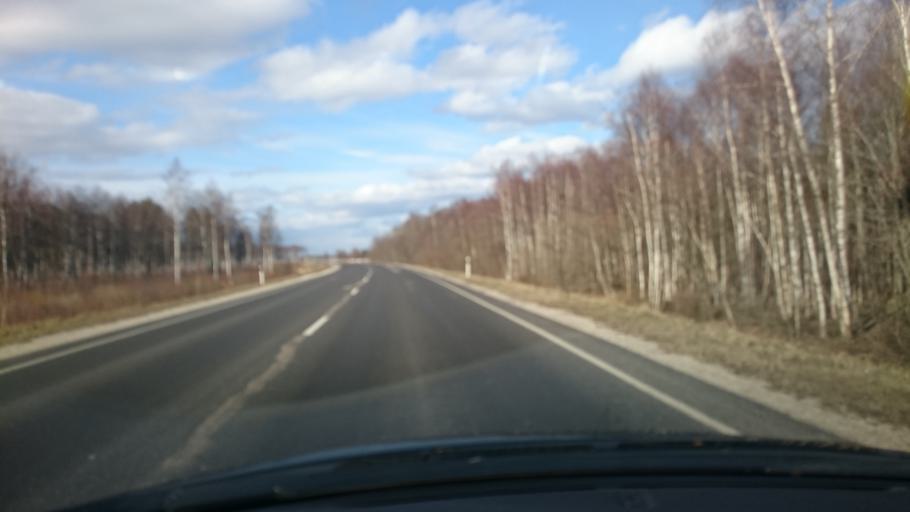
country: EE
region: Laeaene
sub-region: Lihula vald
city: Lihula
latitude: 58.8502
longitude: 24.0680
